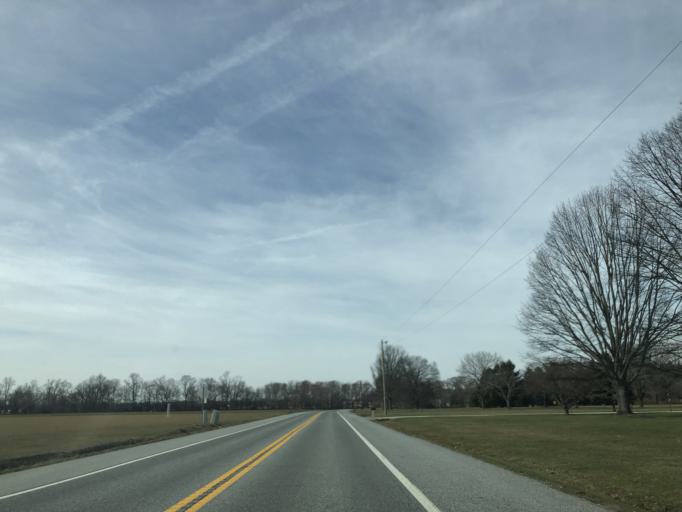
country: US
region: Delaware
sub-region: Kent County
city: Smyrna
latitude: 39.2826
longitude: -75.5720
